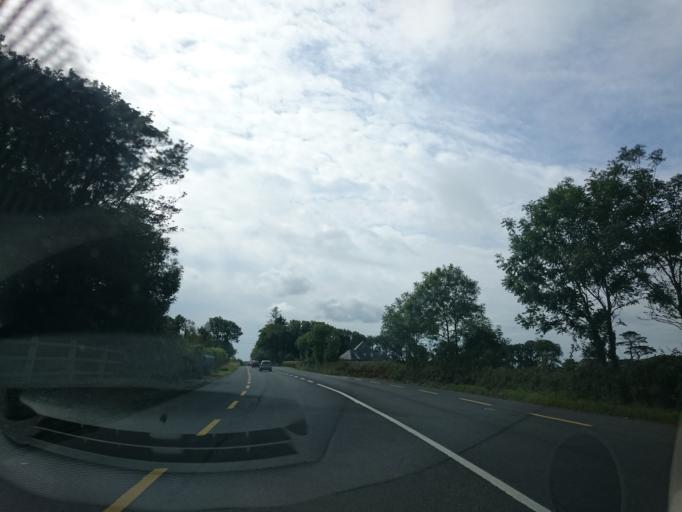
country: IE
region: Munster
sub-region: Waterford
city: Tra Mhor
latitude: 52.2073
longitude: -7.1960
